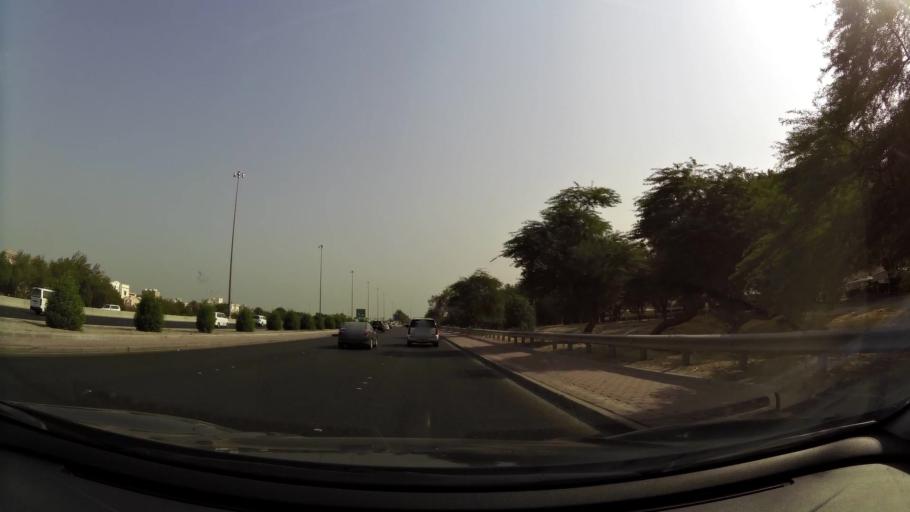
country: KW
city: Bayan
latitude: 29.3084
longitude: 48.0571
